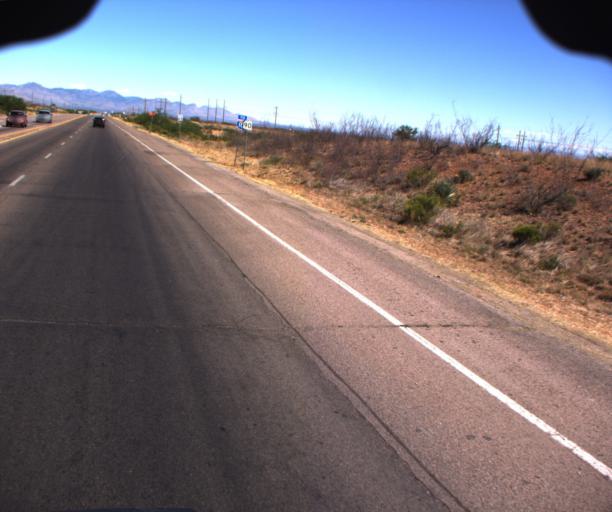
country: US
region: Arizona
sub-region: Cochise County
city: Sierra Vista
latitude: 31.5745
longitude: -110.3154
